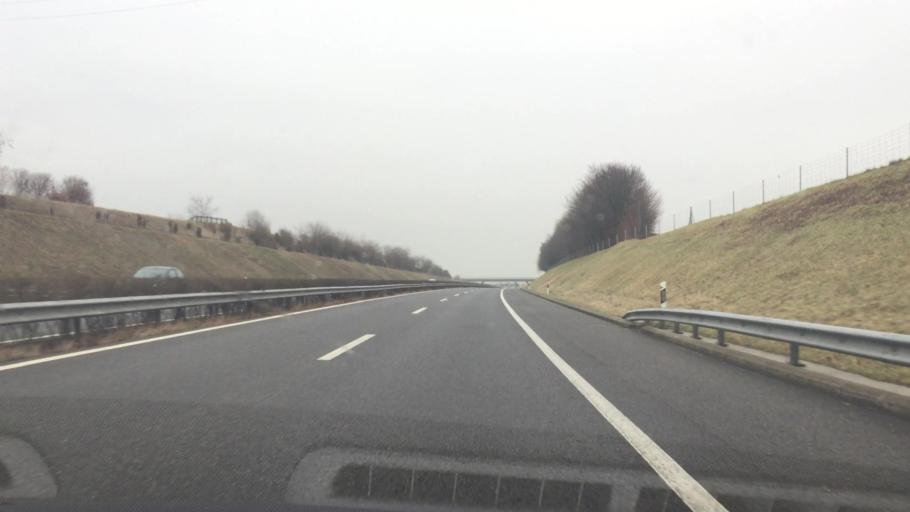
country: CH
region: Vaud
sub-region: Jura-Nord vaudois District
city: Grandson
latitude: 46.8104
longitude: 6.6357
